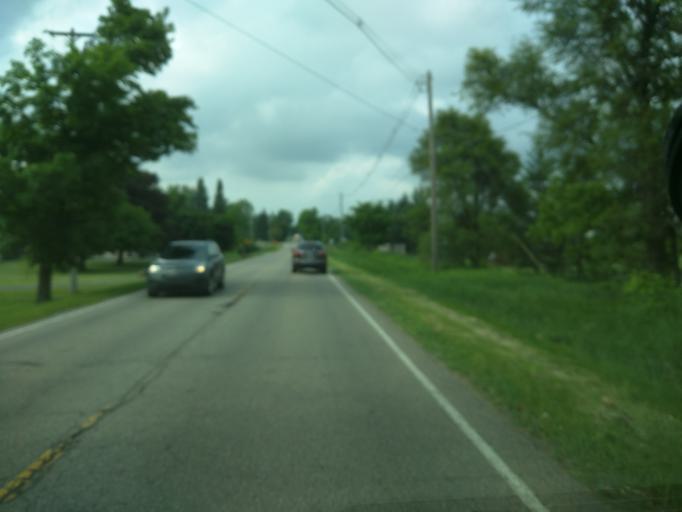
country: US
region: Michigan
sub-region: Ingham County
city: Edgemont Park
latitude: 42.7949
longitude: -84.6028
